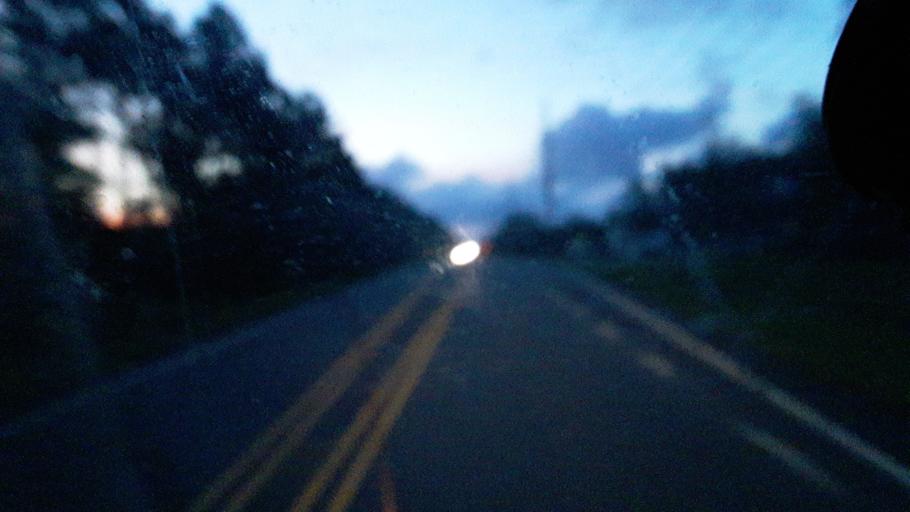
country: US
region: North Carolina
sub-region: Brunswick County
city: Oak Island
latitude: 33.9926
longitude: -78.2166
